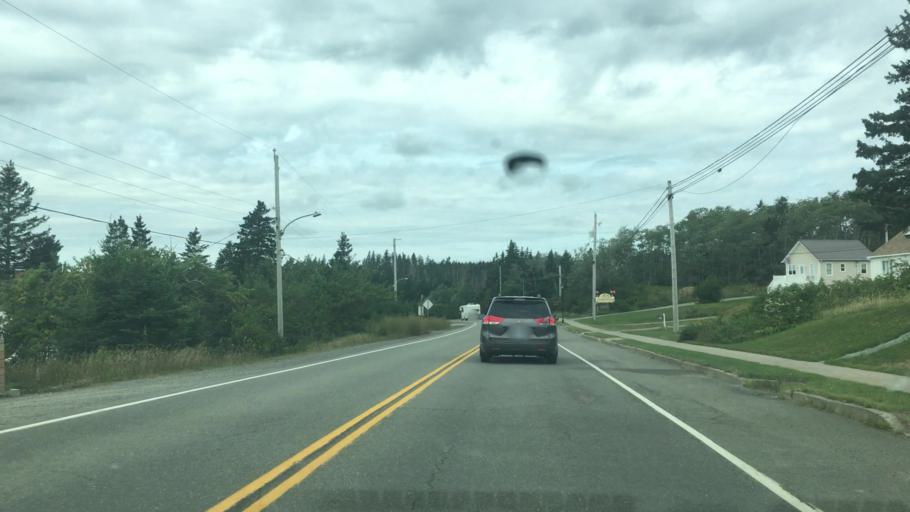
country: CA
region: Nova Scotia
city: Princeville
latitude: 45.6548
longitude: -60.8935
